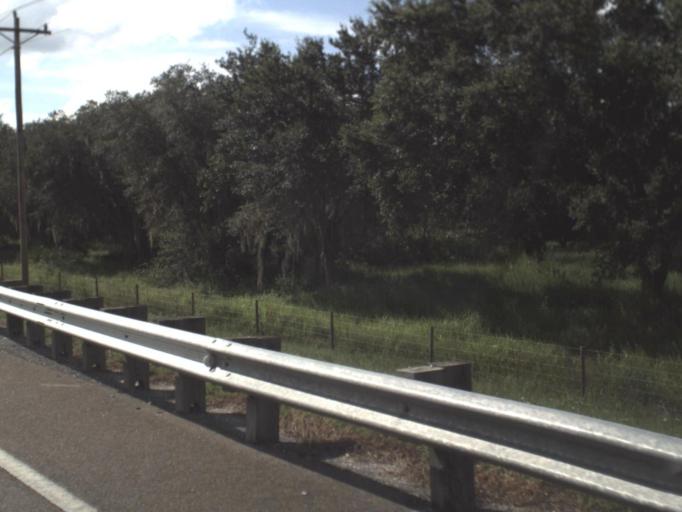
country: US
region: Florida
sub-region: Hardee County
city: Wauchula
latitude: 27.4872
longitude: -82.0239
